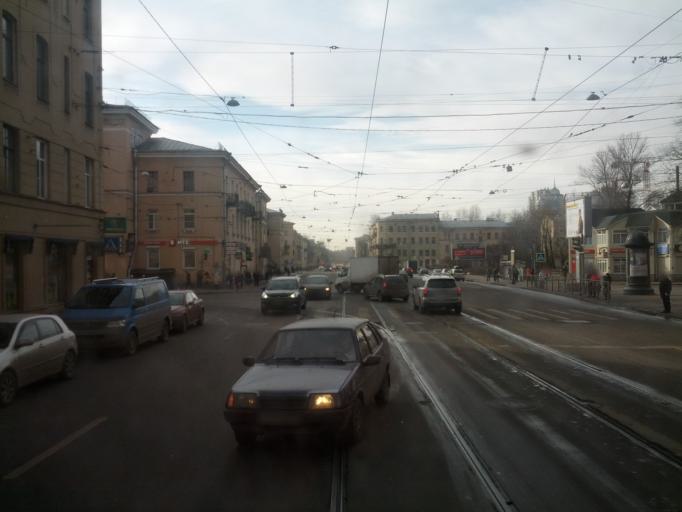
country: RU
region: Leningrad
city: Kalininskiy
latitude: 59.9538
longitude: 30.4151
